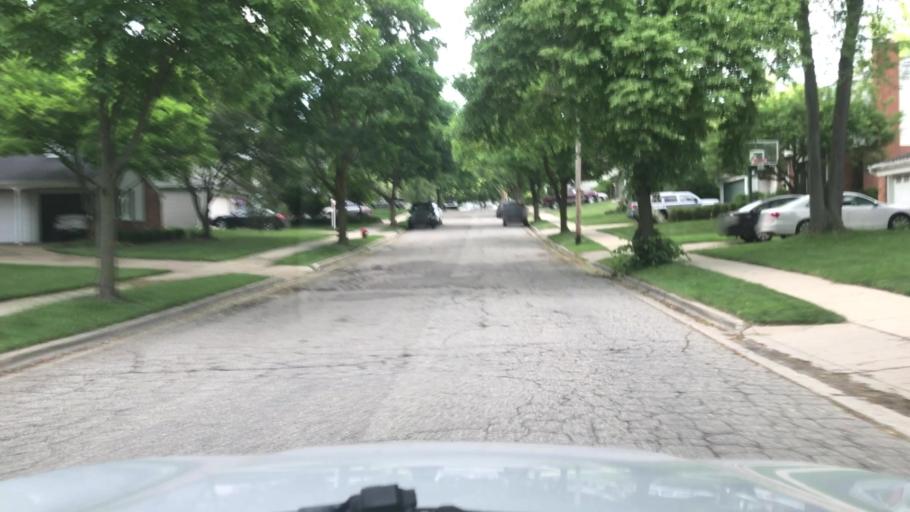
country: US
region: Michigan
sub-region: Wayne County
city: Northville
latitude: 42.4417
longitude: -83.4785
